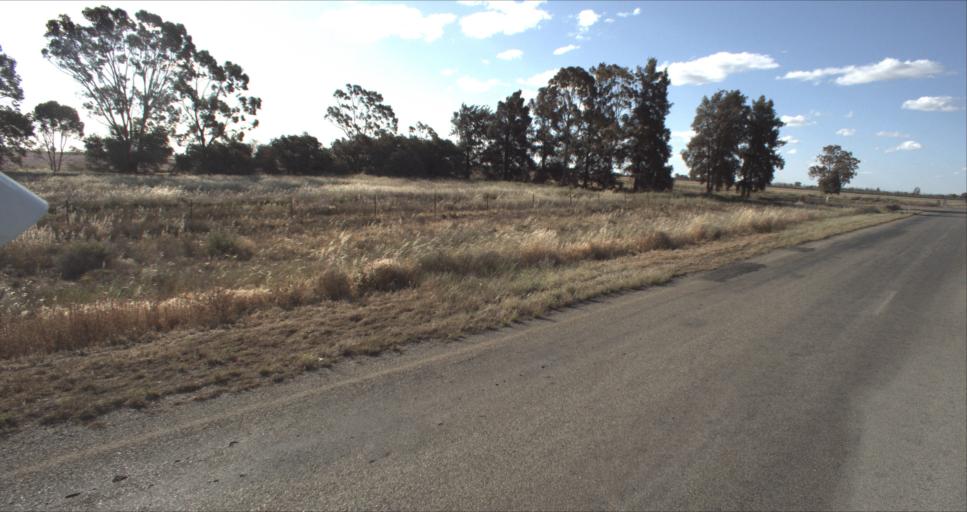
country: AU
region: New South Wales
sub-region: Leeton
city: Leeton
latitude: -34.5388
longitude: 146.2801
